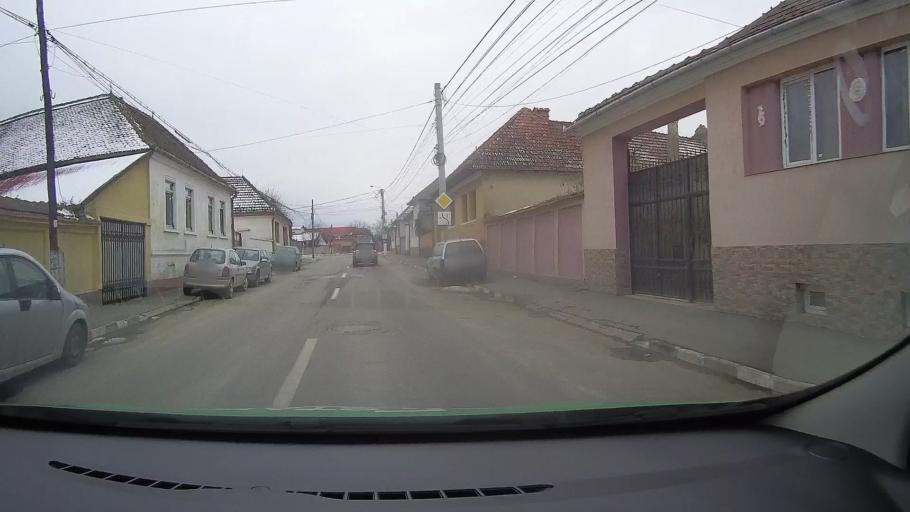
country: RO
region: Brasov
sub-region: Oras Rasnov
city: Rasnov
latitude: 45.5783
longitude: 25.4567
